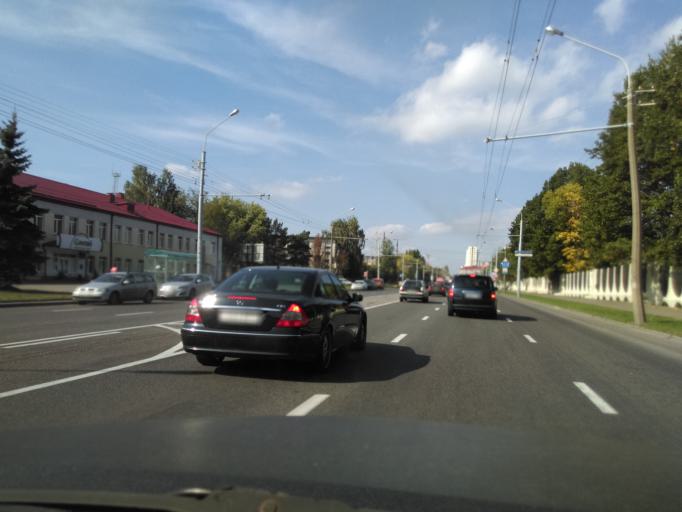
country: BY
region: Minsk
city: Minsk
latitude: 53.9096
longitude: 27.6106
